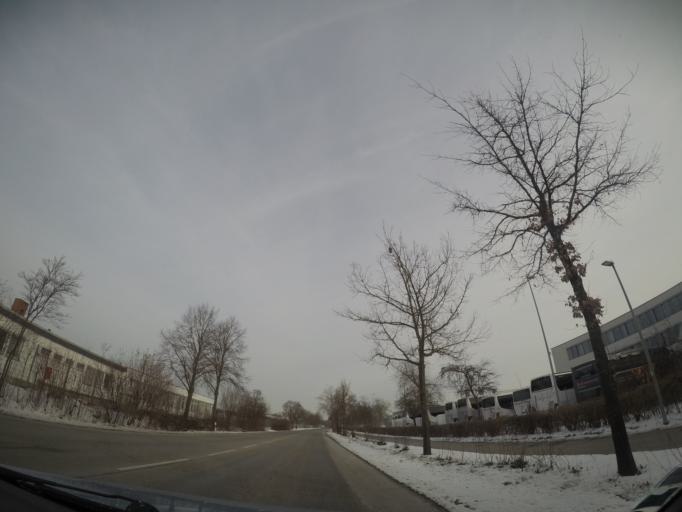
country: DE
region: Bavaria
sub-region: Swabia
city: Neu-Ulm
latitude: 48.3911
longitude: 10.0364
